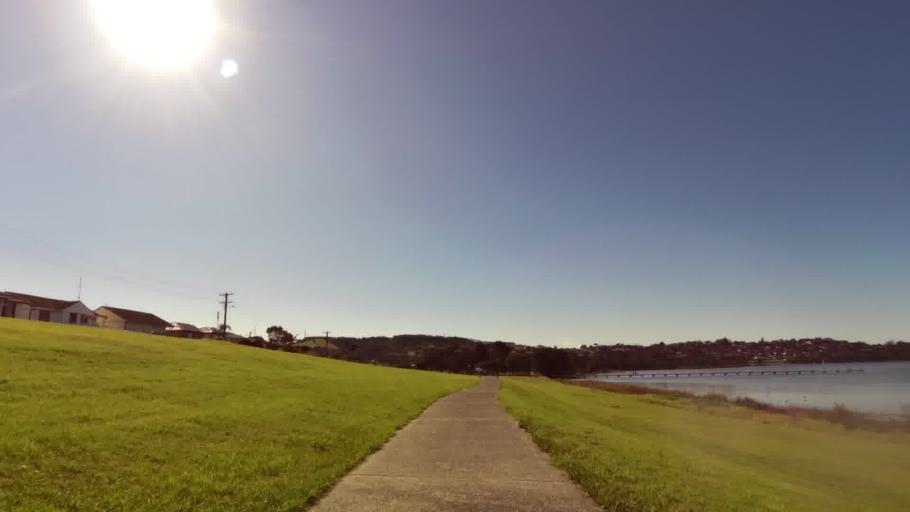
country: AU
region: New South Wales
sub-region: Wollongong
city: Berkeley
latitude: -34.4855
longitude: 150.8432
